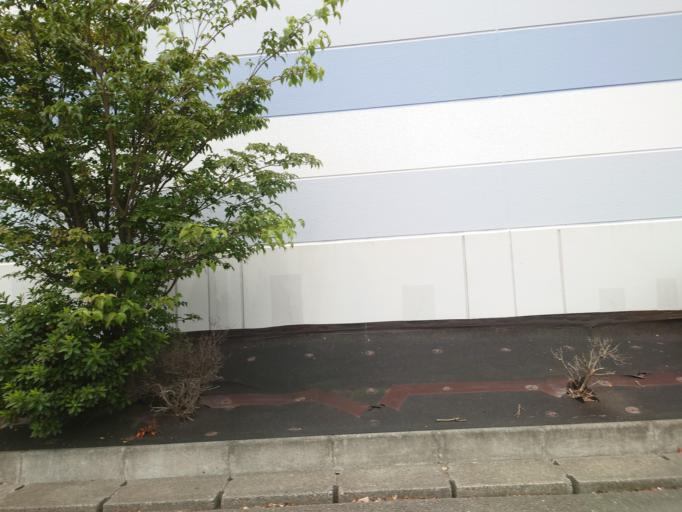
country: JP
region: Tokyo
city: Fussa
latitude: 35.7934
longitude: 139.3031
